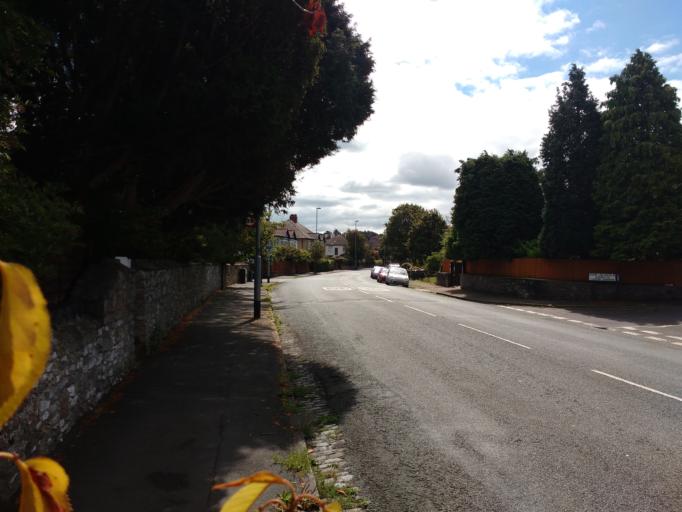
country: GB
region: England
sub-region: Bristol
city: Bristol
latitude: 51.4877
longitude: -2.6321
